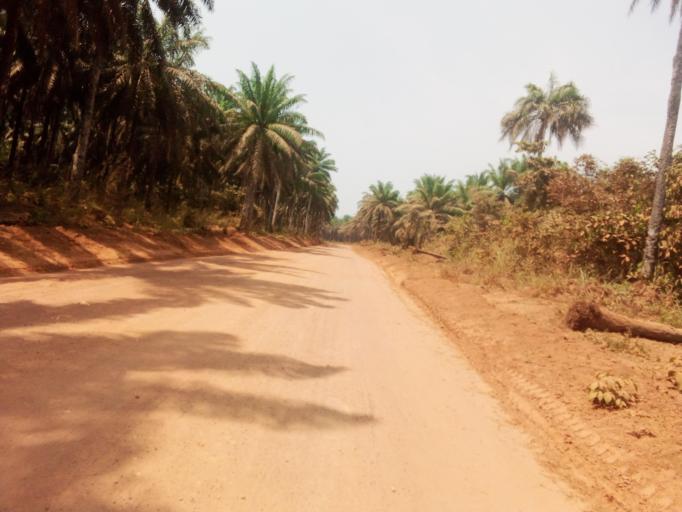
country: SL
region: Southern Province
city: Sumbuya
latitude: 7.6200
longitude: -12.1212
